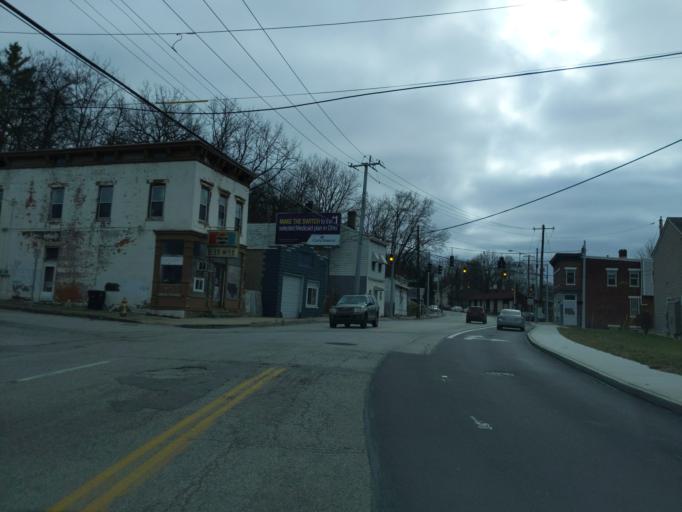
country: US
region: Ohio
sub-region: Hamilton County
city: Finneytown
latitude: 39.1719
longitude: -84.5470
